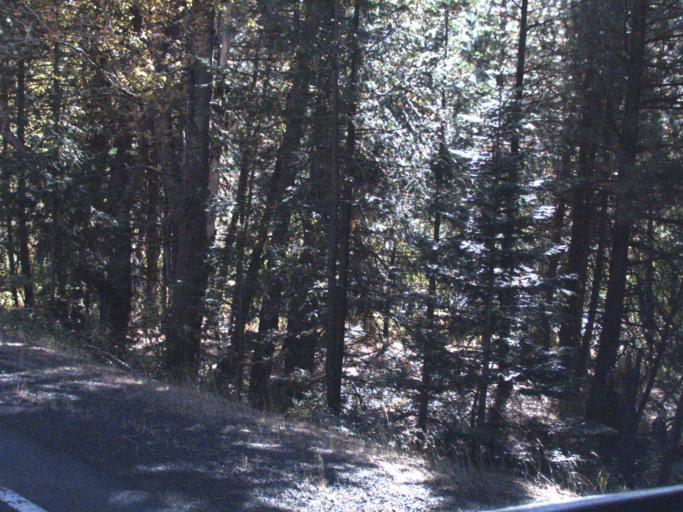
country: US
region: Washington
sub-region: Yakima County
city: Tieton
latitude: 46.6750
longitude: -121.0610
